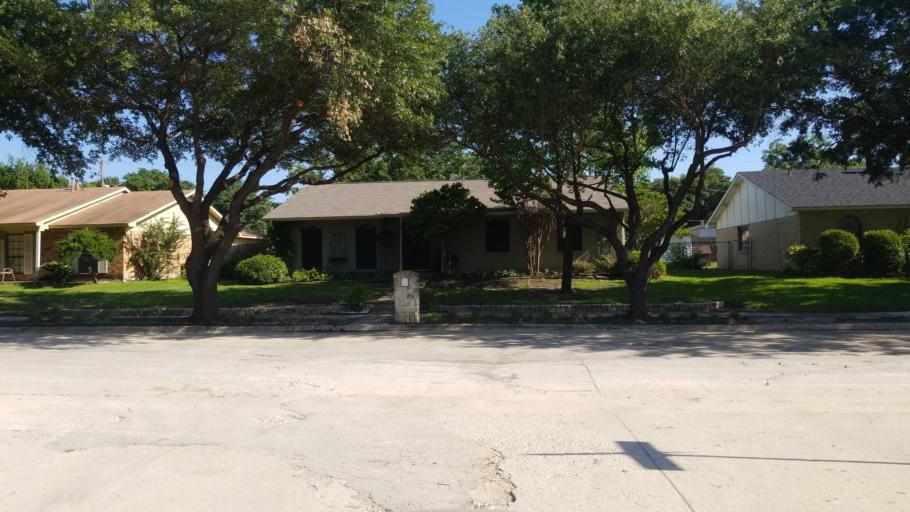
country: US
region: Texas
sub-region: Dallas County
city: Grand Prairie
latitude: 32.6835
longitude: -97.0134
